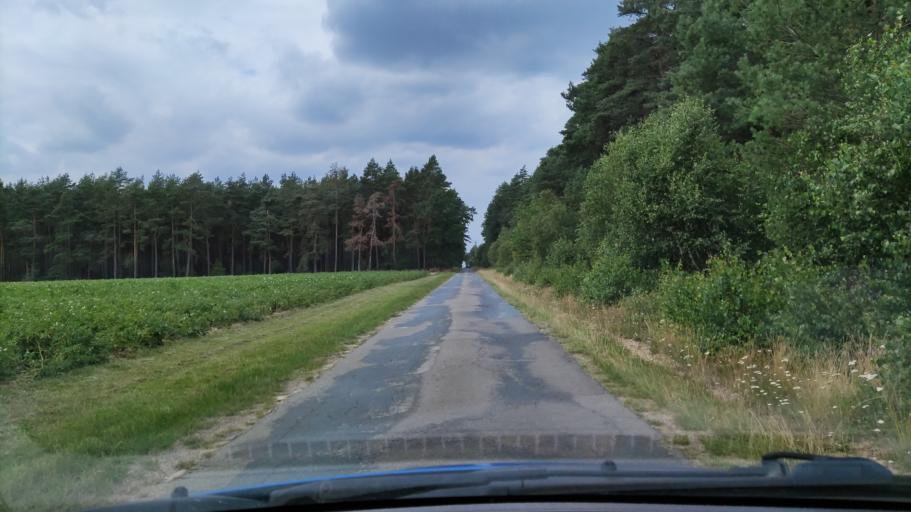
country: DE
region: Lower Saxony
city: Schnega
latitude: 52.9466
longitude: 10.8608
